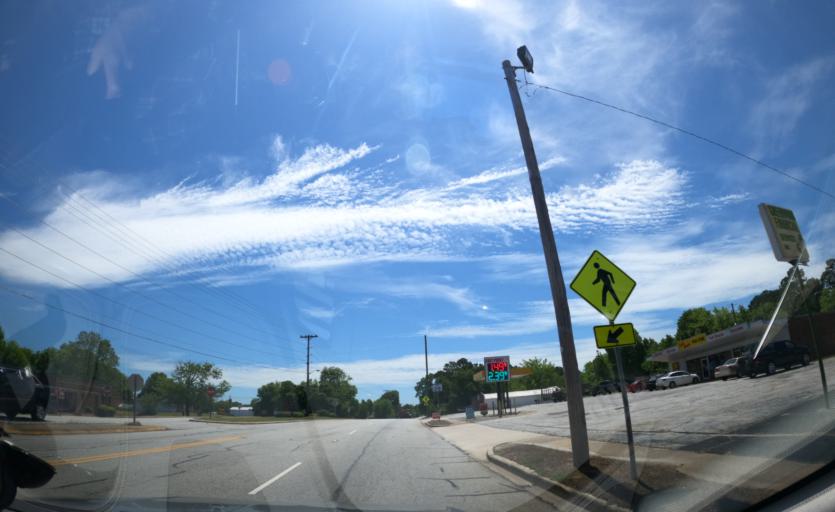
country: US
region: South Carolina
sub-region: McCormick County
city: McCormick
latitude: 33.9131
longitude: -82.2979
